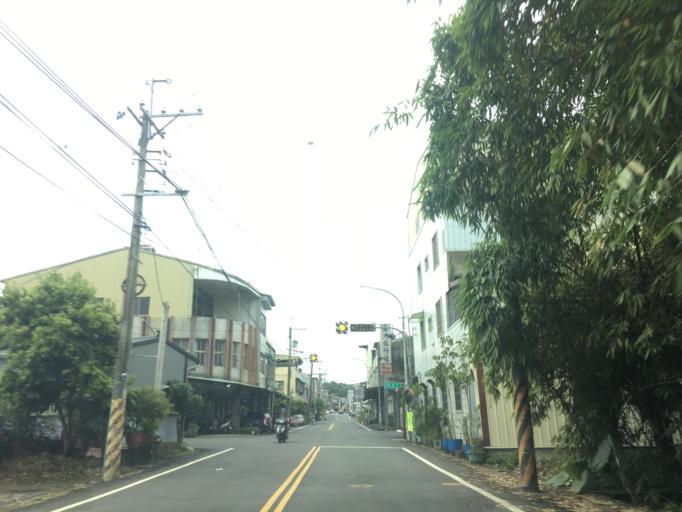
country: TW
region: Taiwan
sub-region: Yunlin
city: Douliu
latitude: 23.5888
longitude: 120.5551
